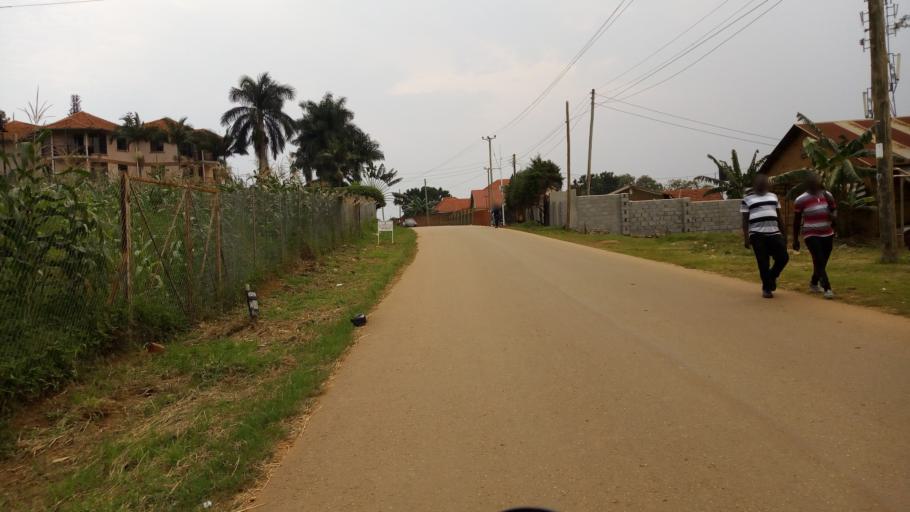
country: UG
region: Central Region
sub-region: Wakiso District
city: Kireka
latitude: 0.3187
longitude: 32.6423
